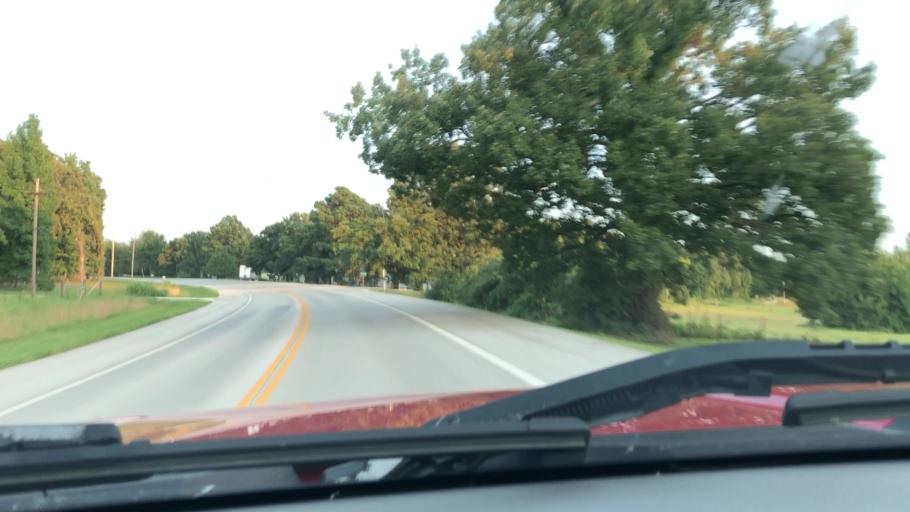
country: US
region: Missouri
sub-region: Jasper County
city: Duquesne
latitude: 36.9773
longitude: -94.4630
